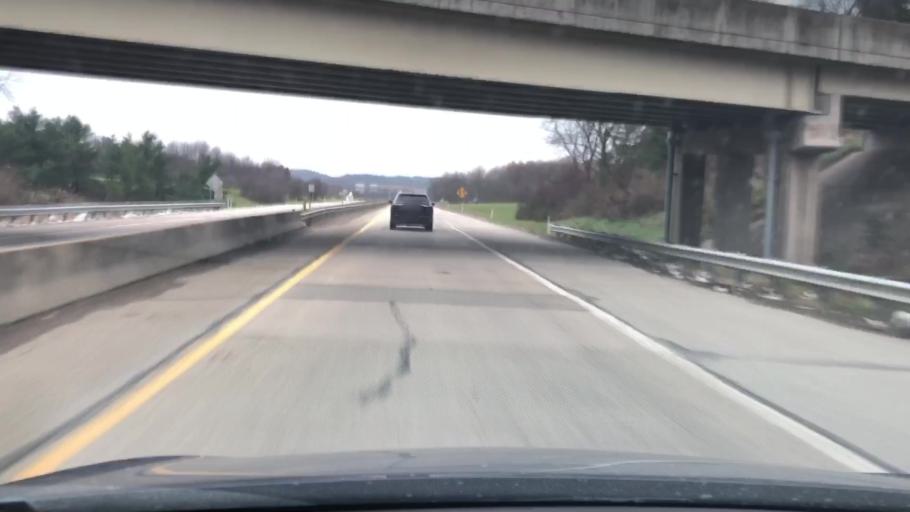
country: US
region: Pennsylvania
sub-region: Armstrong County
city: West Hills
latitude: 40.8106
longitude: -79.5534
